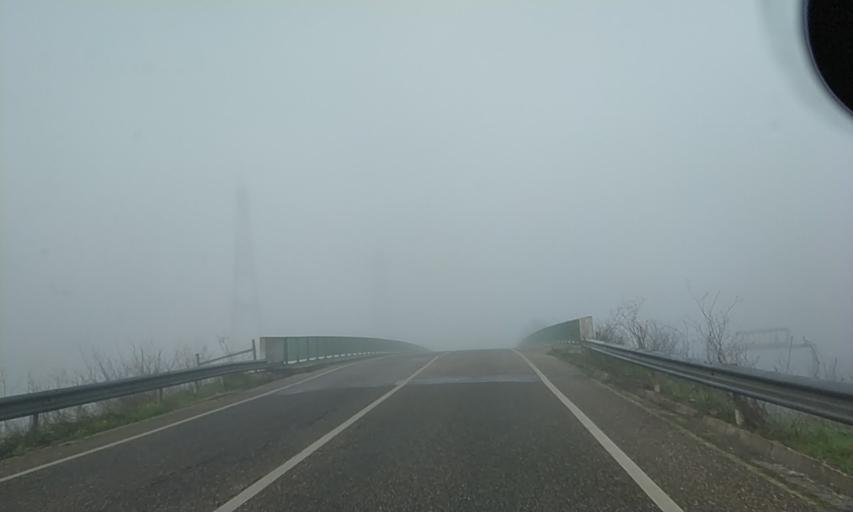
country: PT
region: Setubal
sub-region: Palmela
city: Pinhal Novo
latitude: 38.6101
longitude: -8.8664
